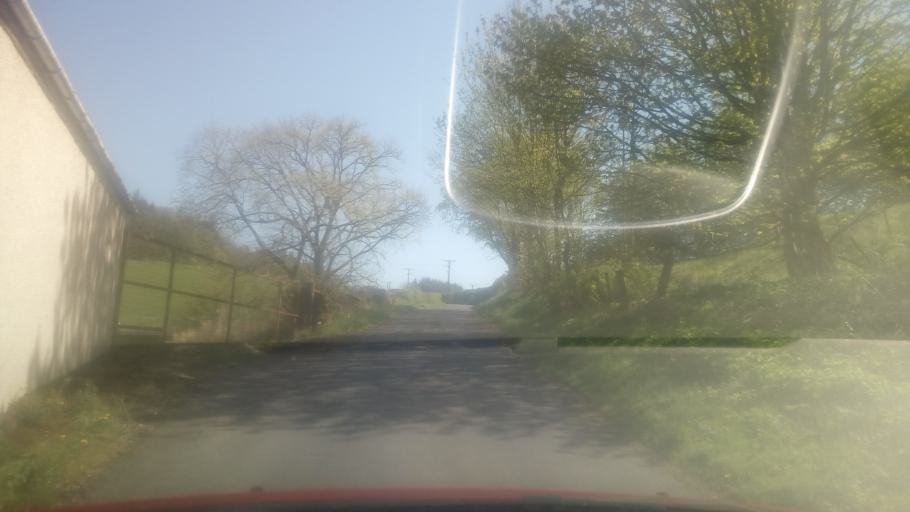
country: GB
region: Scotland
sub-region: The Scottish Borders
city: Hawick
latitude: 55.4504
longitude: -2.7195
